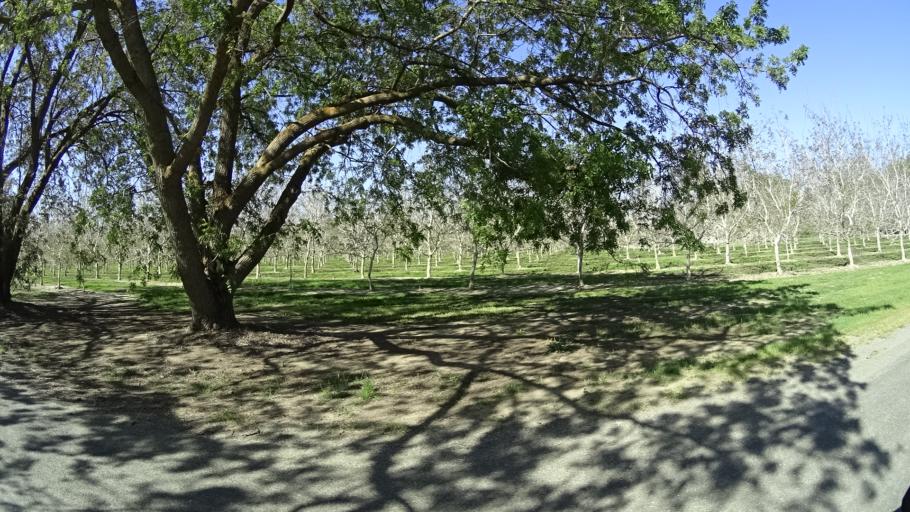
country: US
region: California
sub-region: Glenn County
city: Hamilton City
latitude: 39.7243
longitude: -122.0129
